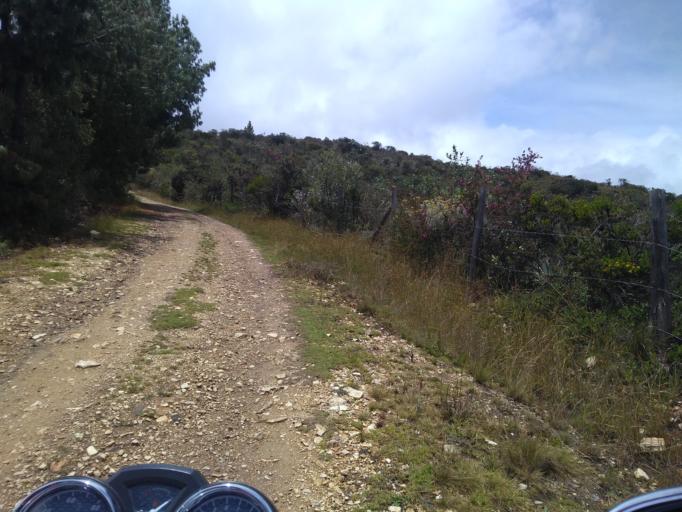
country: CO
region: Boyaca
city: Toca
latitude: 5.5871
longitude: -73.1256
